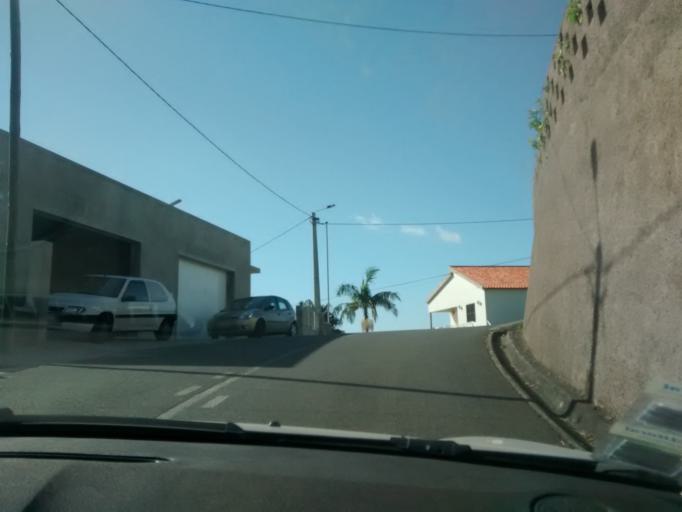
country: PT
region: Madeira
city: Calheta
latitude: 32.7219
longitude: -17.1724
